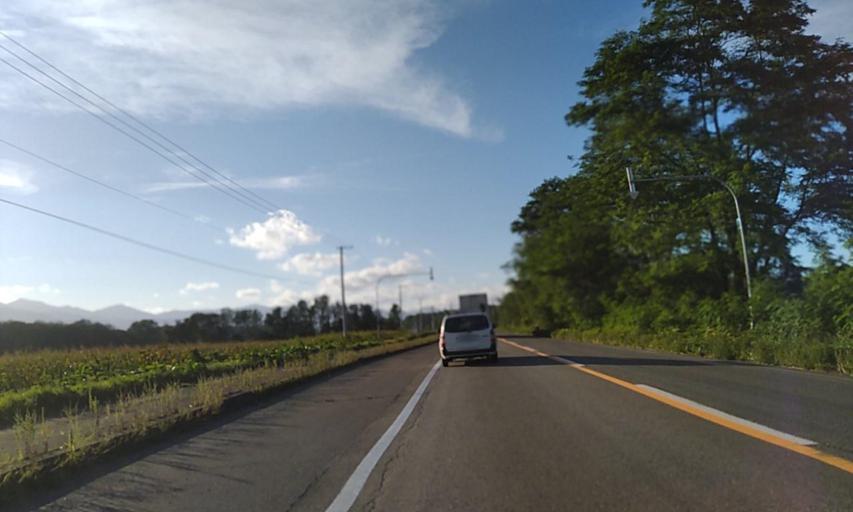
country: JP
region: Hokkaido
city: Obihiro
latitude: 42.9302
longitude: 142.9799
